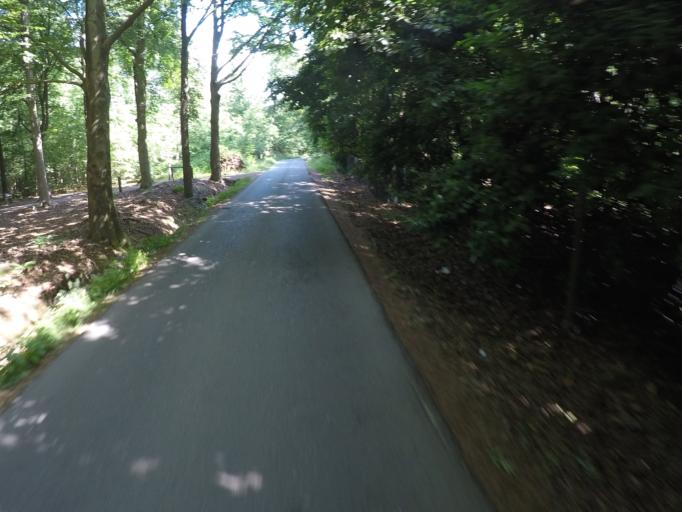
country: BE
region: Flanders
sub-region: Provincie Antwerpen
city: Kalmthout
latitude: 51.3748
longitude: 4.5335
